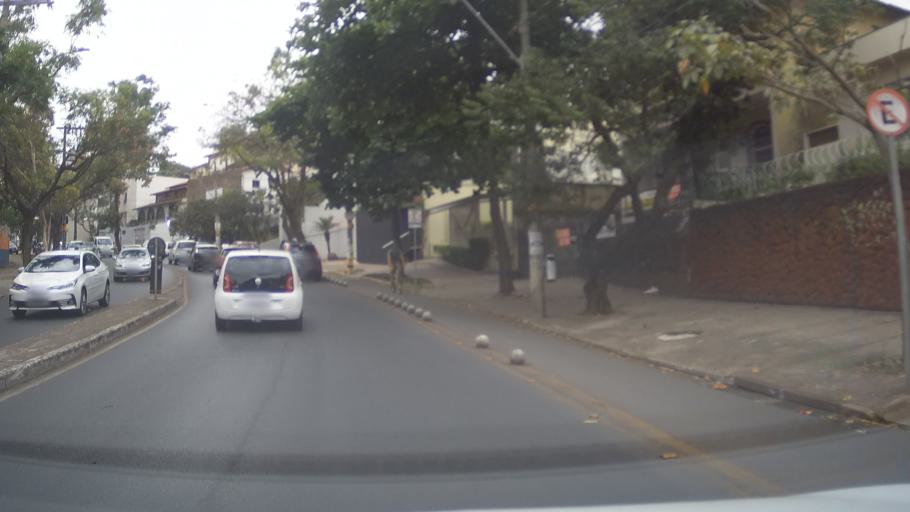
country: BR
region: Minas Gerais
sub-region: Belo Horizonte
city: Belo Horizonte
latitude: -19.9520
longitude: -43.9227
